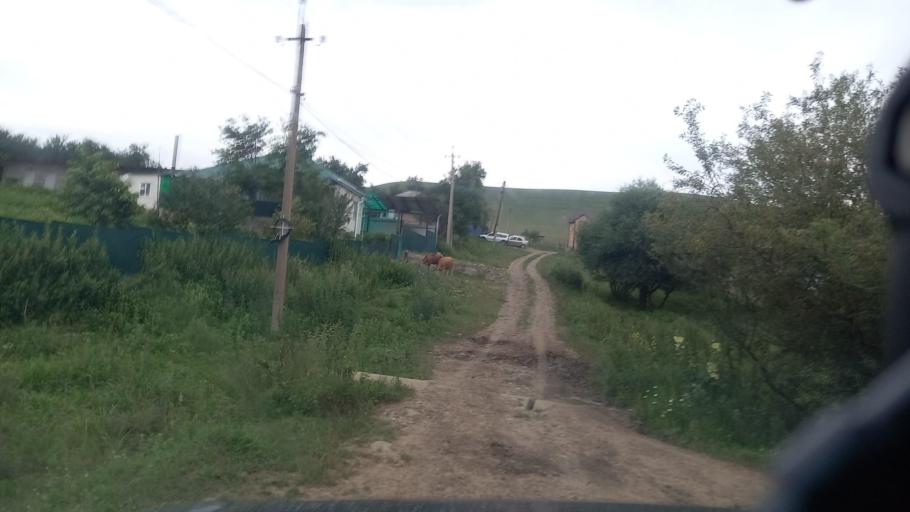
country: RU
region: Karachayevo-Cherkesiya
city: Pregradnaya
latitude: 43.9504
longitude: 41.1713
